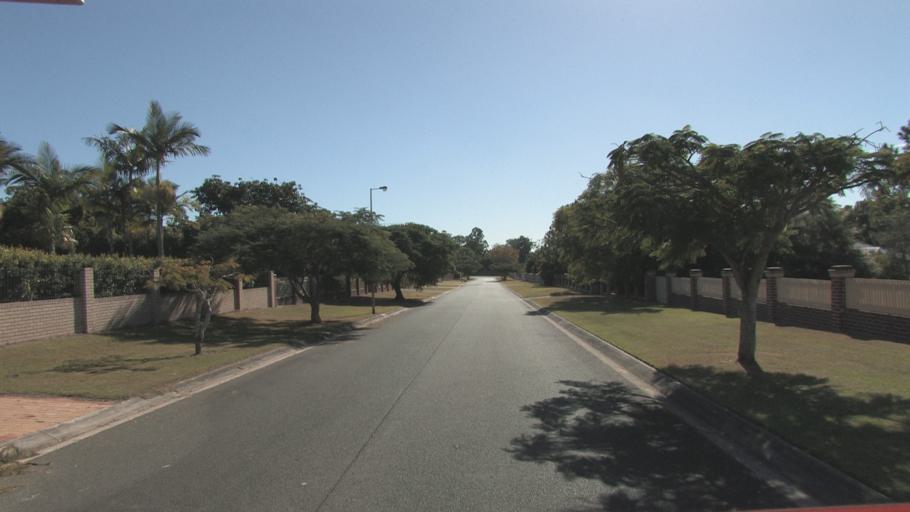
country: AU
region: Queensland
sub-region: Brisbane
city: Forest Lake
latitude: -27.6657
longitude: 153.0139
